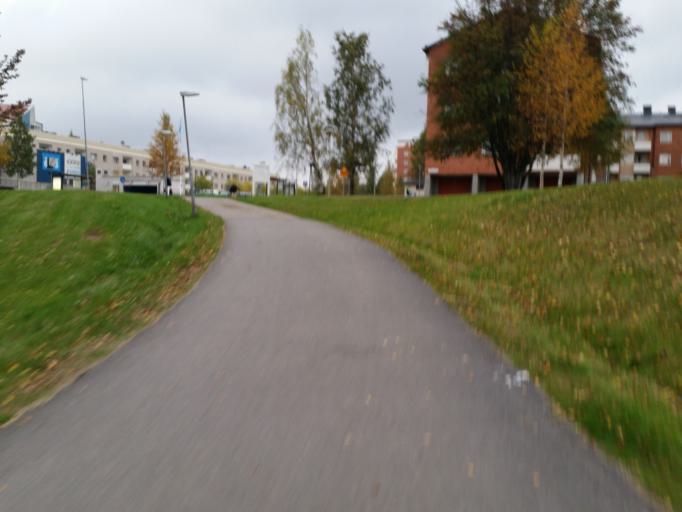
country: SE
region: Norrbotten
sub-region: Lulea Kommun
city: Lulea
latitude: 65.5779
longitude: 22.1992
